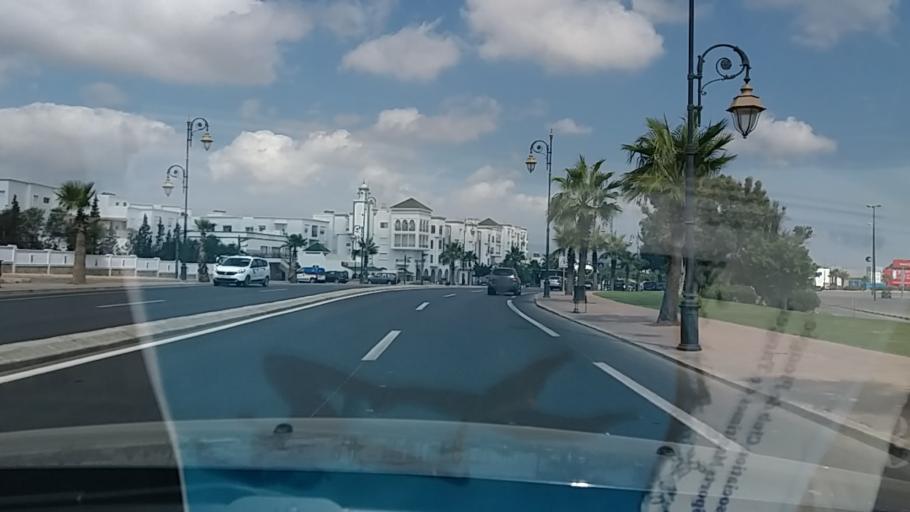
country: MA
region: Tanger-Tetouan
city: Tetouan
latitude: 35.6017
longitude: -5.3365
